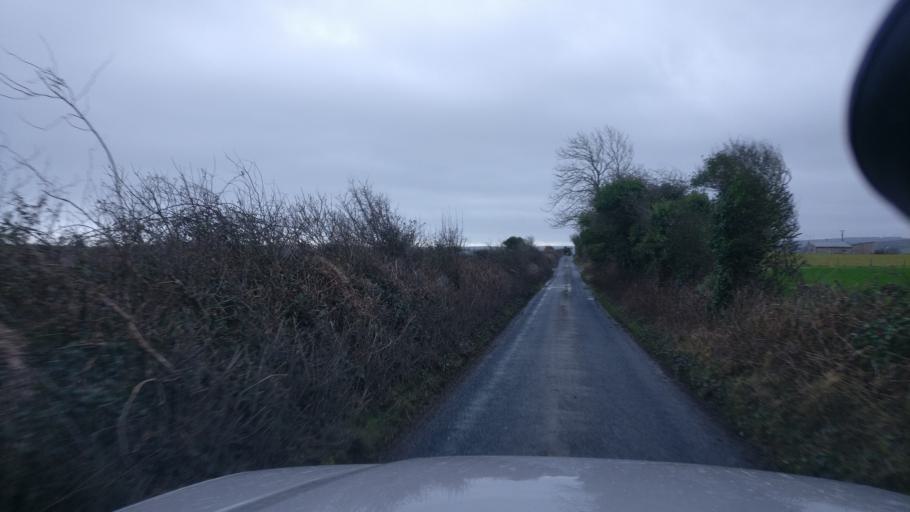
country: IE
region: Connaught
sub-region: County Galway
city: Loughrea
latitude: 53.2064
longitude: -8.6637
